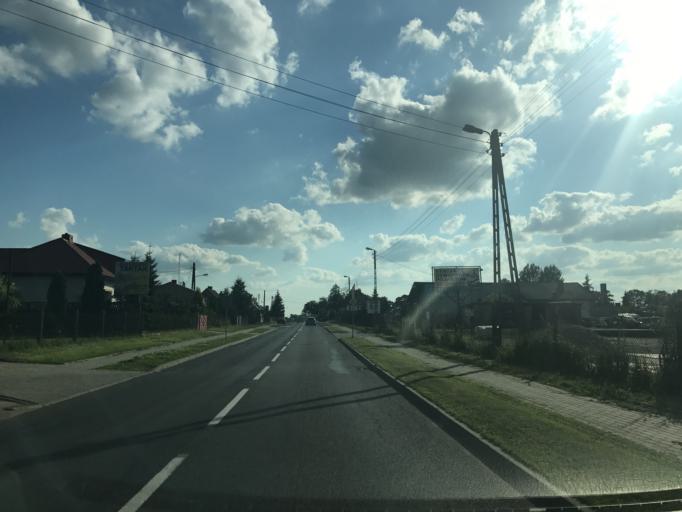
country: PL
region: Kujawsko-Pomorskie
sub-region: Powiat wloclawski
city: Izbica Kujawska
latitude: 52.4164
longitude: 18.7582
